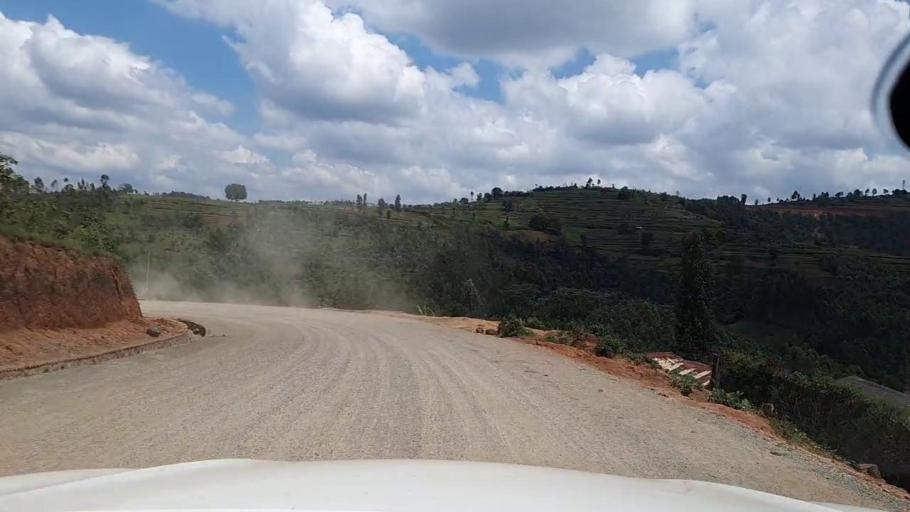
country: RW
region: Southern Province
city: Butare
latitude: -2.6943
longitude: 29.5588
